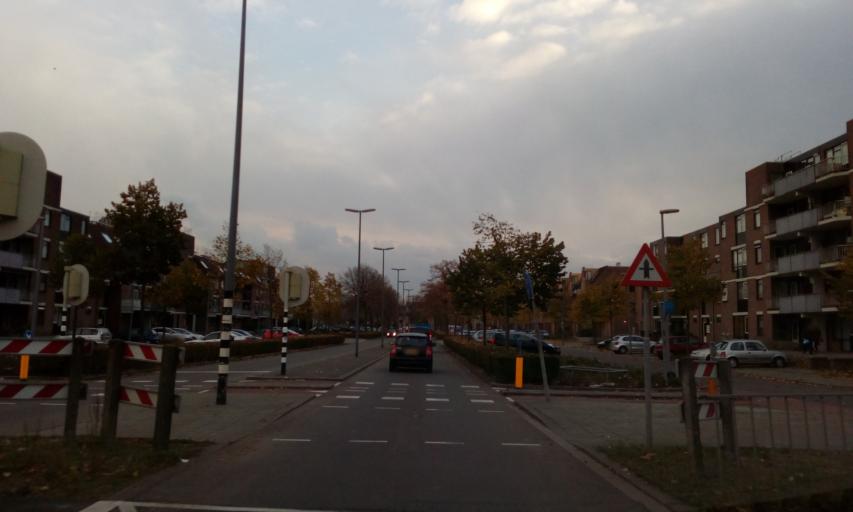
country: NL
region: South Holland
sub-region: Gemeente Capelle aan den IJssel
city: Capelle aan den IJssel
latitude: 51.9651
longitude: 4.5625
